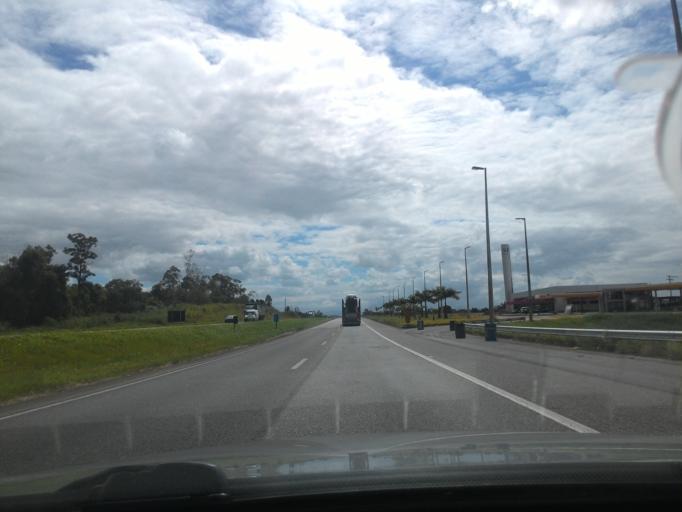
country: BR
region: Sao Paulo
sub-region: Jacupiranga
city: Jacupiranga
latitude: -24.6512
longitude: -47.9437
